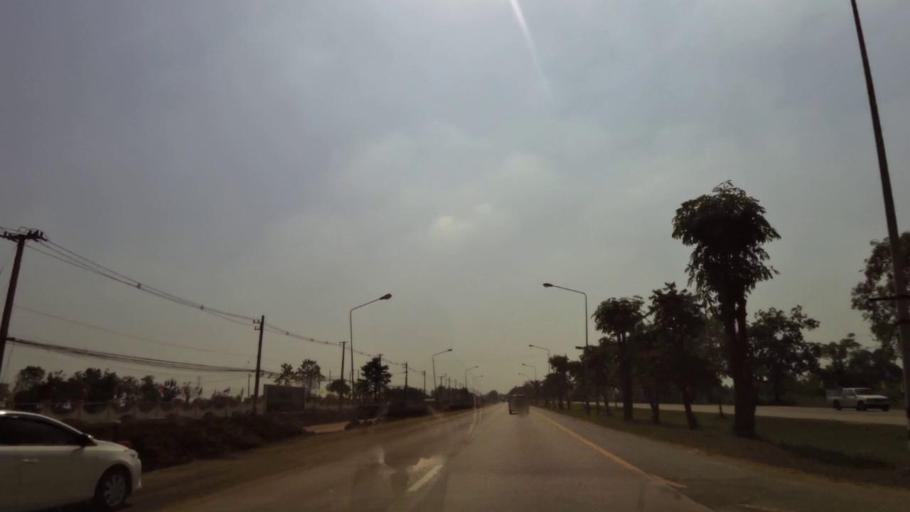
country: TH
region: Phichit
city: Wachira Barami
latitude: 16.5242
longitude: 100.1431
